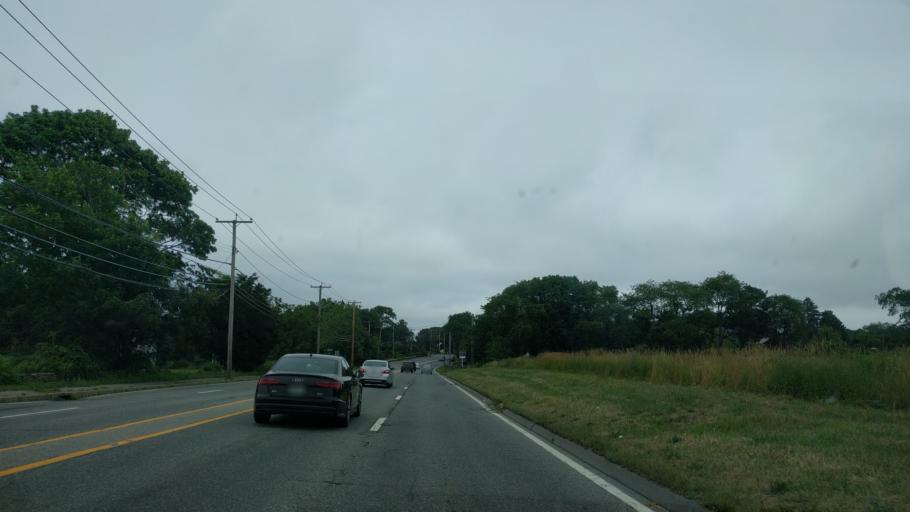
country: US
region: Rhode Island
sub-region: Newport County
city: Middletown
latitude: 41.5519
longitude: -71.2914
